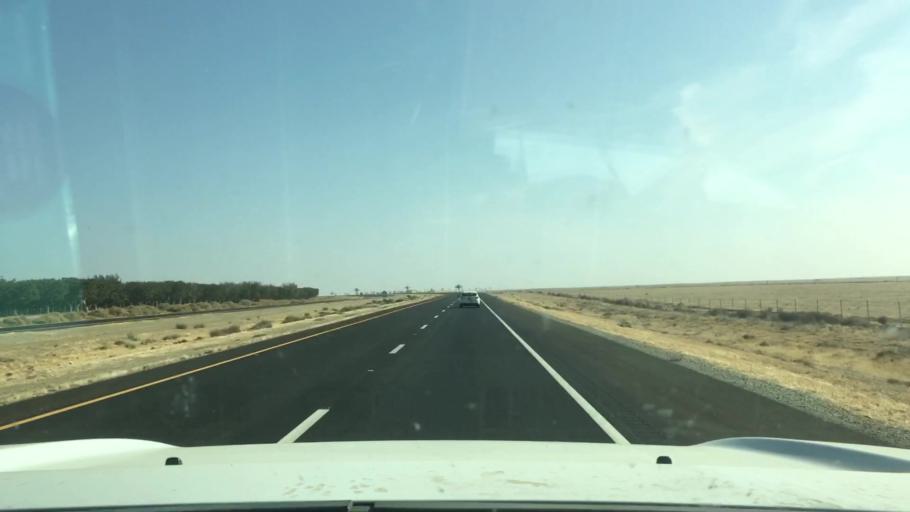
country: US
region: California
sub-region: Kern County
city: Lost Hills
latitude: 35.6164
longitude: -119.9691
